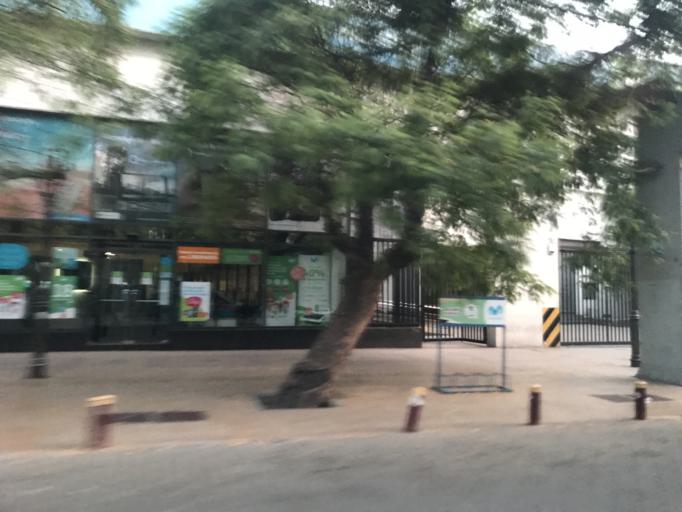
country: AR
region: Mendoza
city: Mendoza
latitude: -32.8908
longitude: -68.8383
